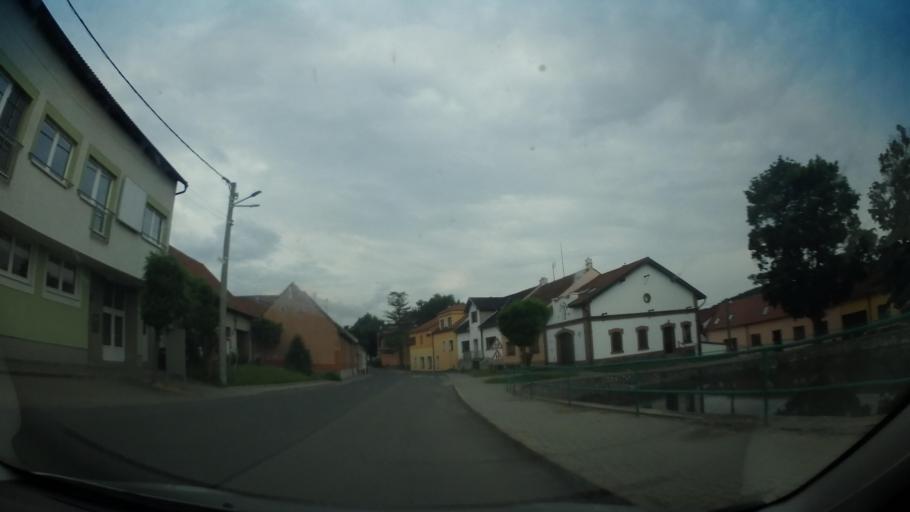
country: CZ
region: South Moravian
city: Cebin
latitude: 49.3126
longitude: 16.4790
